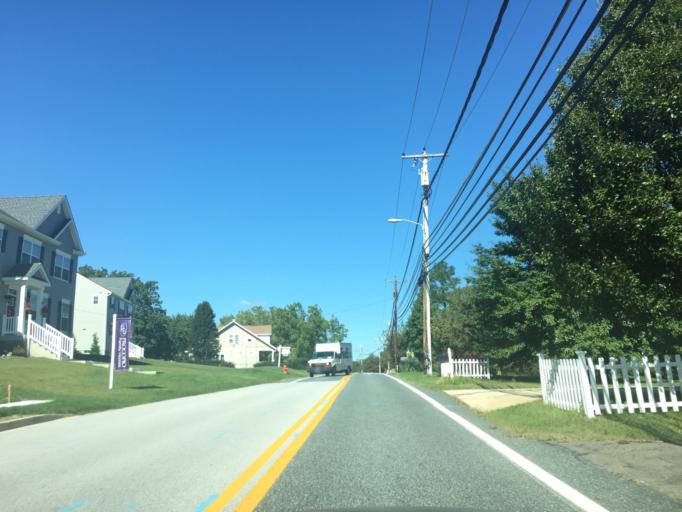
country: US
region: Maryland
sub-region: Baltimore County
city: Overlea
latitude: 39.3701
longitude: -76.4989
